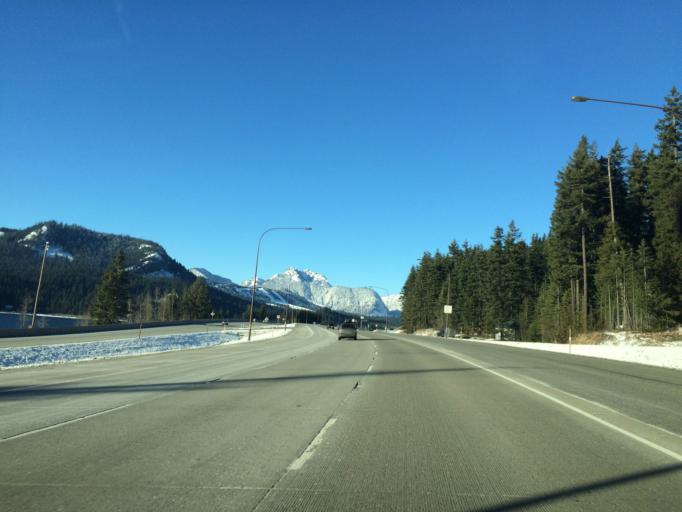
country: US
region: Washington
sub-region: King County
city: Tanner
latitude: 47.3686
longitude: -121.3729
